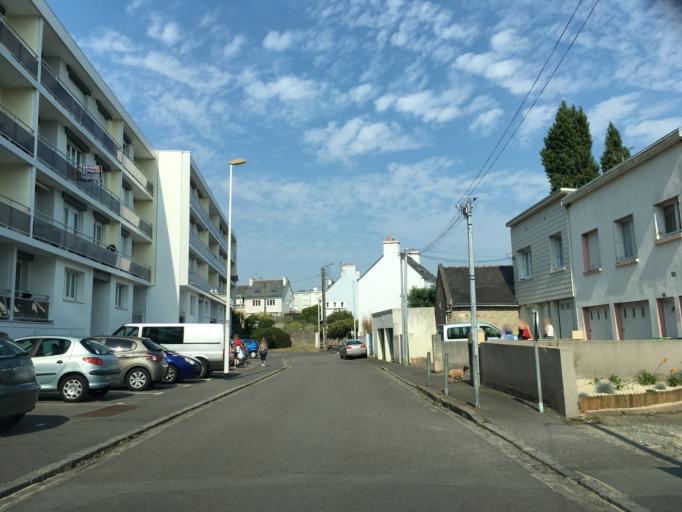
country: FR
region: Brittany
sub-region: Departement du Morbihan
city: Lorient
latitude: 47.7568
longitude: -3.3796
